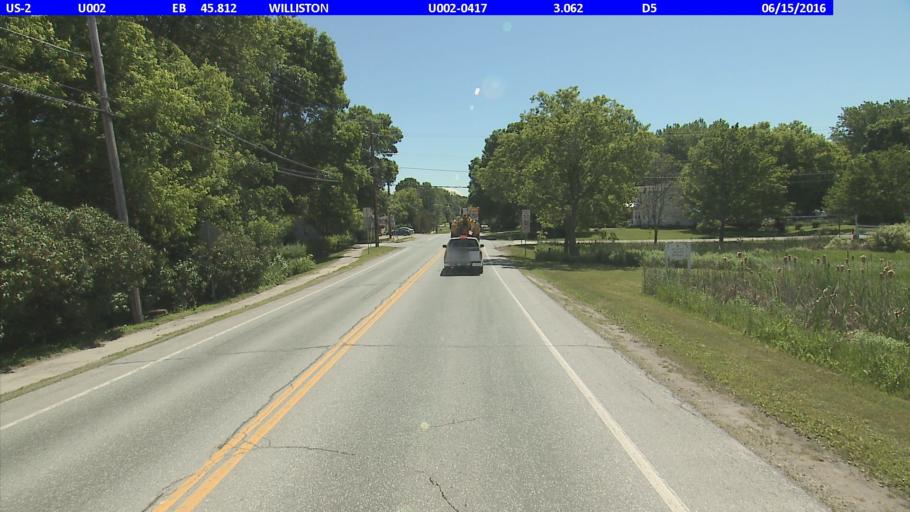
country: US
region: Vermont
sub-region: Chittenden County
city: Williston
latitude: 44.4402
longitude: -73.0814
